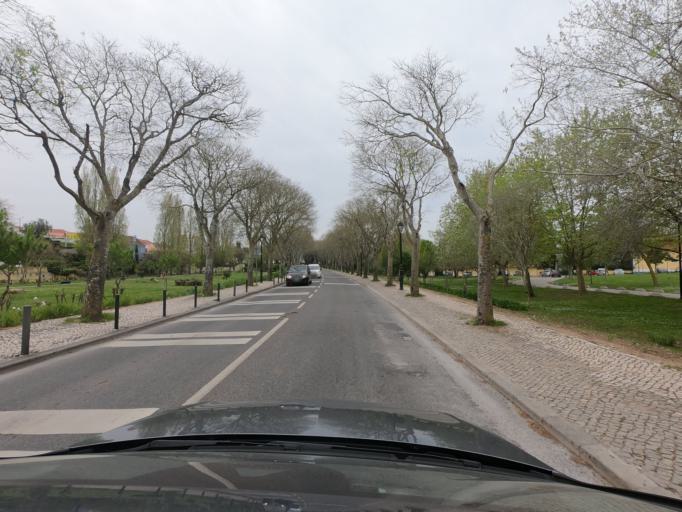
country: PT
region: Lisbon
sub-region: Sintra
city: Queluz
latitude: 38.7536
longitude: -9.2596
